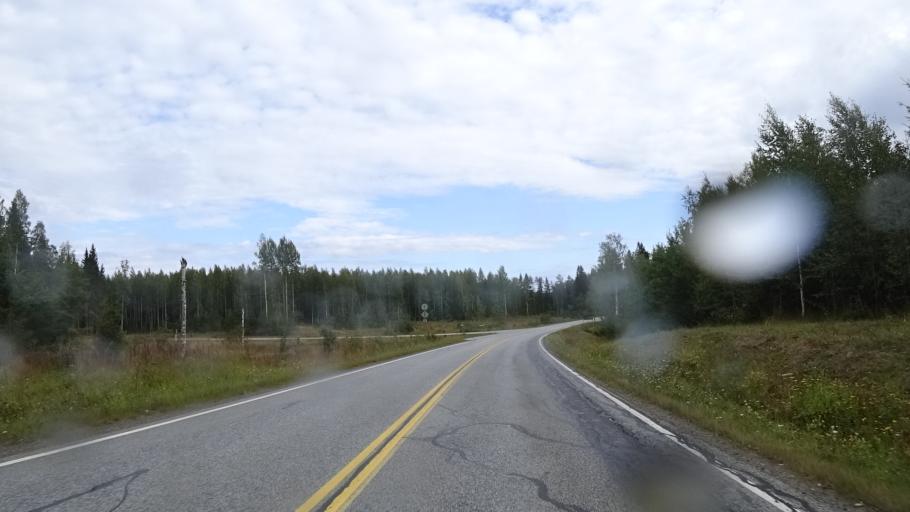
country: FI
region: North Karelia
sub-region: Keski-Karjala
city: Raeaekkylae
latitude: 62.1036
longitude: 29.6775
